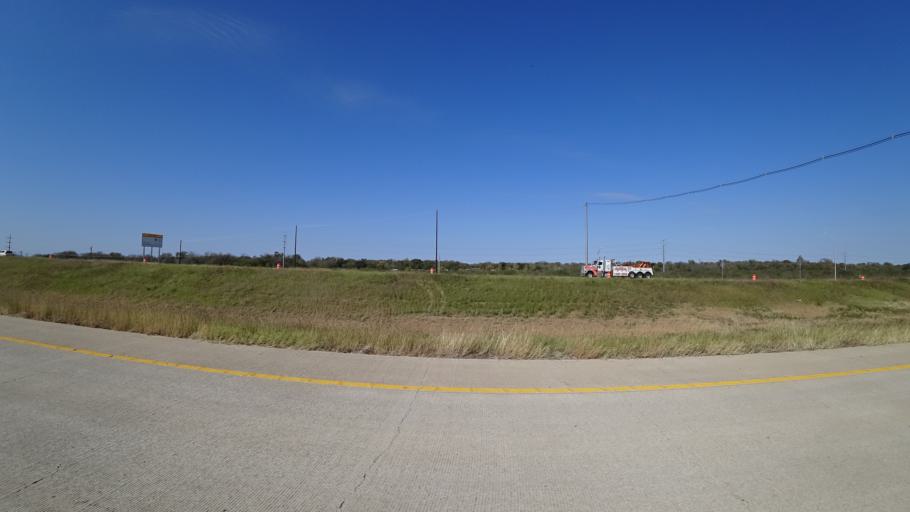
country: US
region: Texas
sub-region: Travis County
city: Garfield
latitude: 30.1776
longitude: -97.6347
